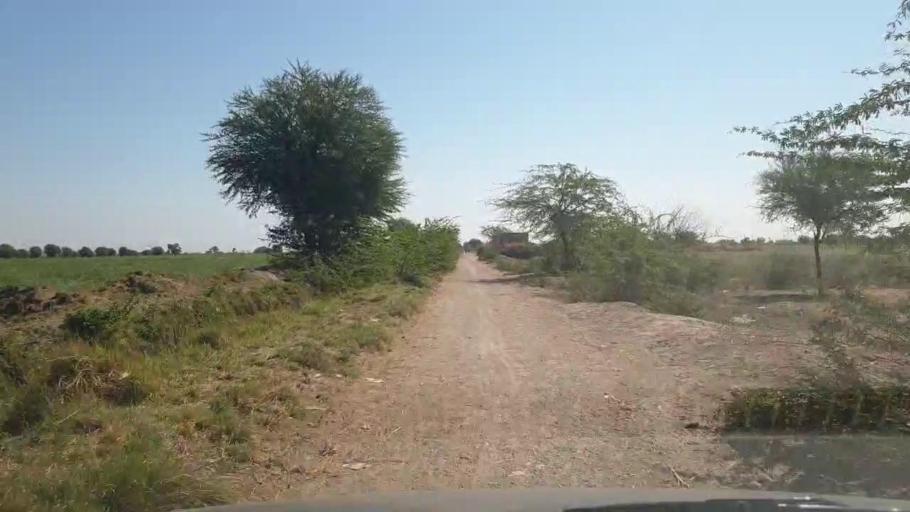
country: PK
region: Sindh
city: Umarkot
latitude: 25.3820
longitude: 69.6256
